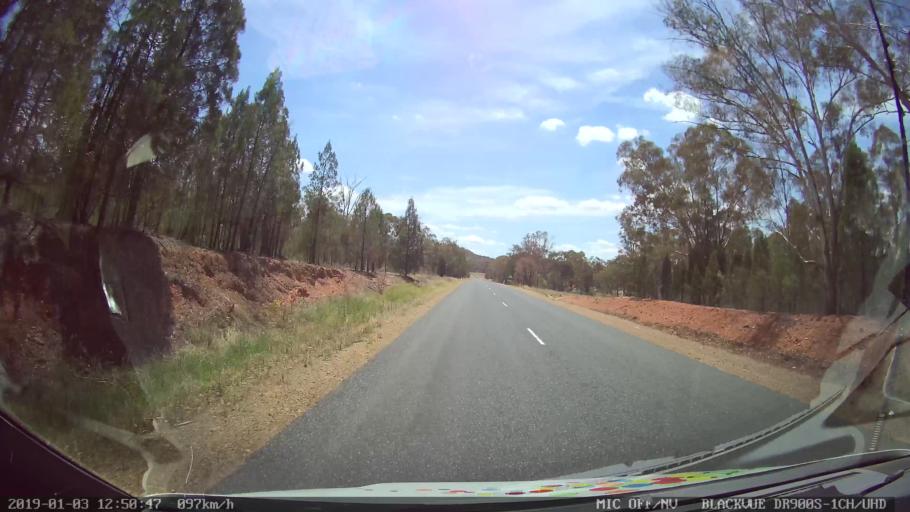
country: AU
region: New South Wales
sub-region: Weddin
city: Grenfell
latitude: -33.6873
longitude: 148.2736
